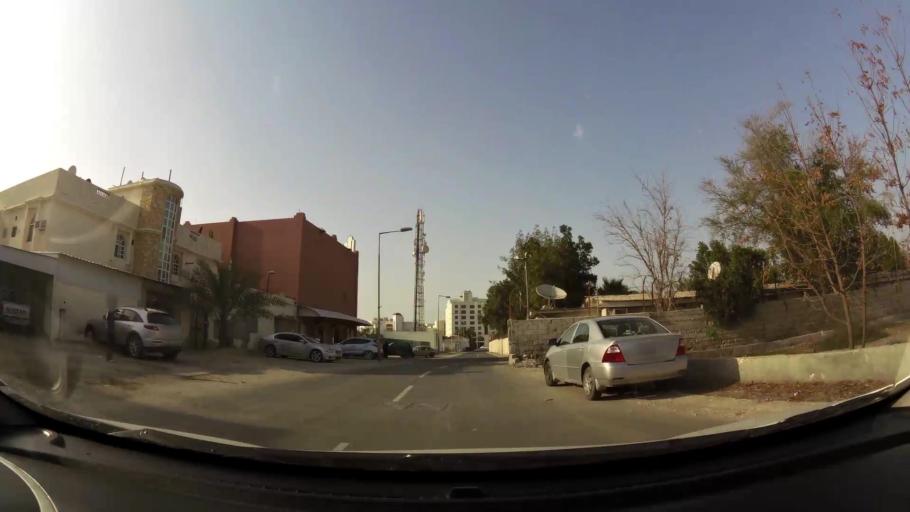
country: BH
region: Manama
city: Jidd Hafs
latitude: 26.2185
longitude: 50.5042
